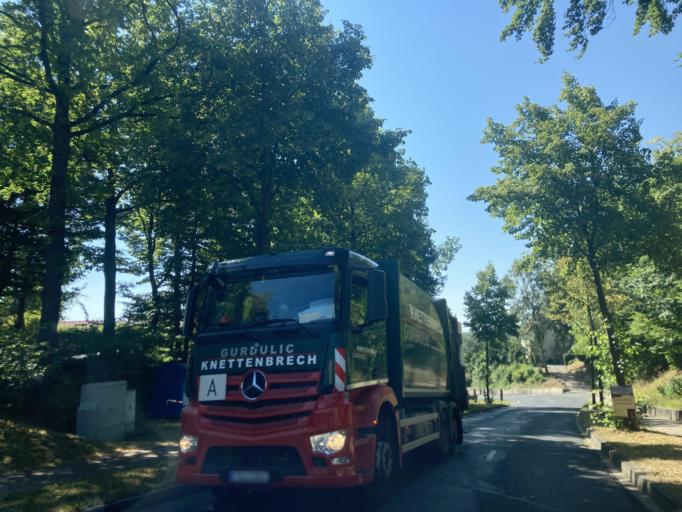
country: DE
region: Hesse
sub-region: Regierungsbezirk Kassel
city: Neuhof
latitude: 50.4582
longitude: 9.6106
